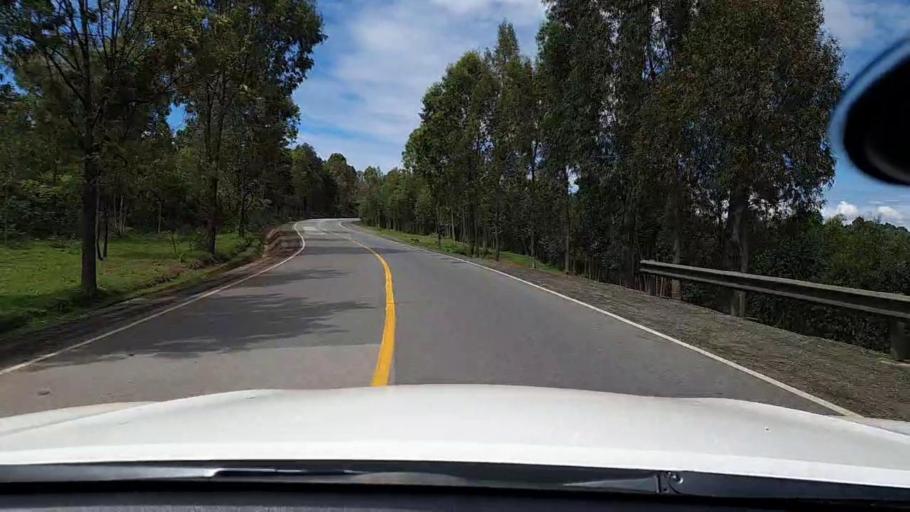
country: RW
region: Kigali
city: Kigali
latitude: -1.8236
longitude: 29.9479
